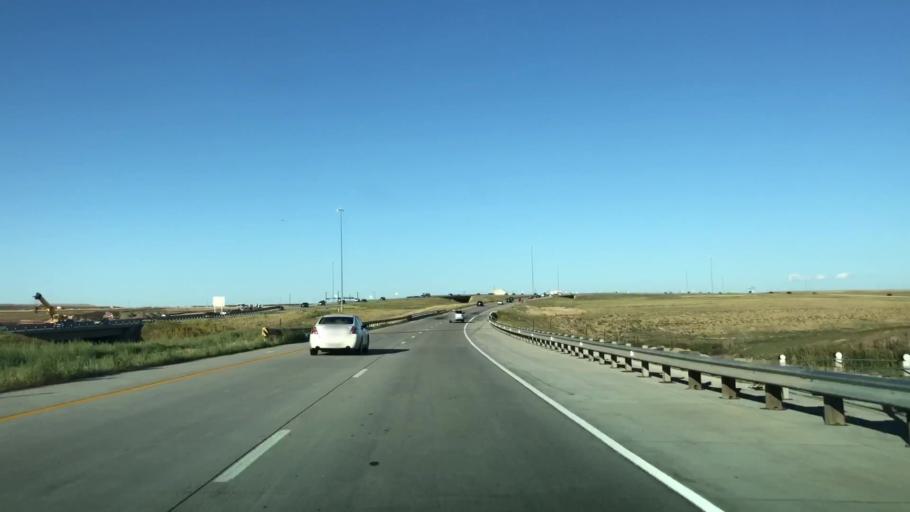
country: US
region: Colorado
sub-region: Adams County
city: Aurora
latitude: 39.8316
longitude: -104.7776
